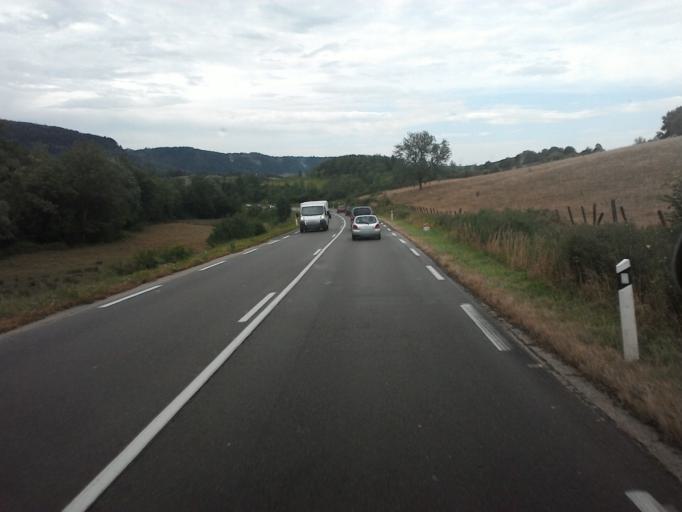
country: FR
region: Franche-Comte
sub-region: Departement du Jura
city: Poligny
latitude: 46.8603
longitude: 5.7127
